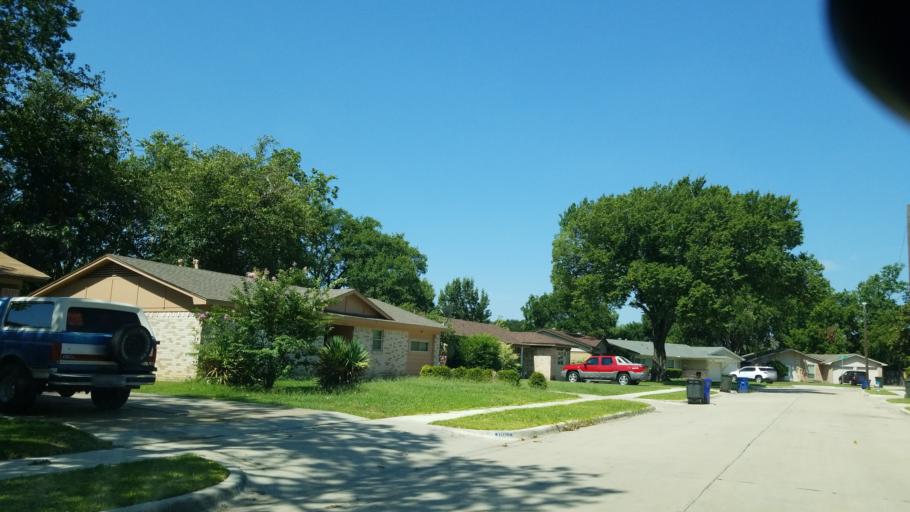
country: US
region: Texas
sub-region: Dallas County
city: Carrollton
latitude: 32.9689
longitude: -96.9044
